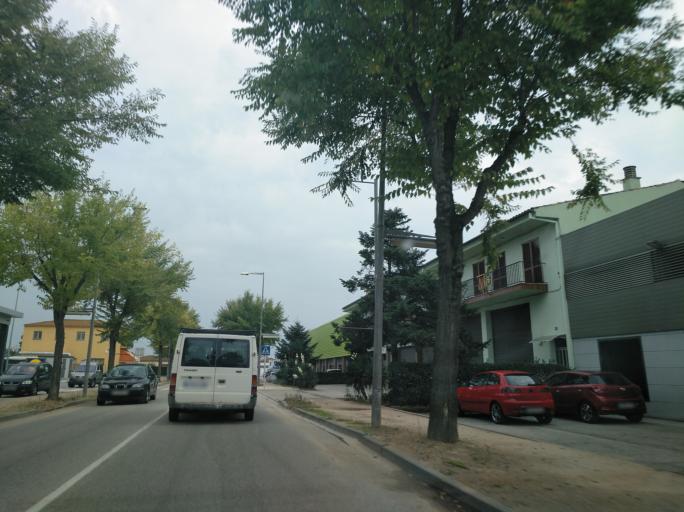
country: ES
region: Catalonia
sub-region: Provincia de Girona
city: Santa Coloma de Farners
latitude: 41.8561
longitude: 2.6768
